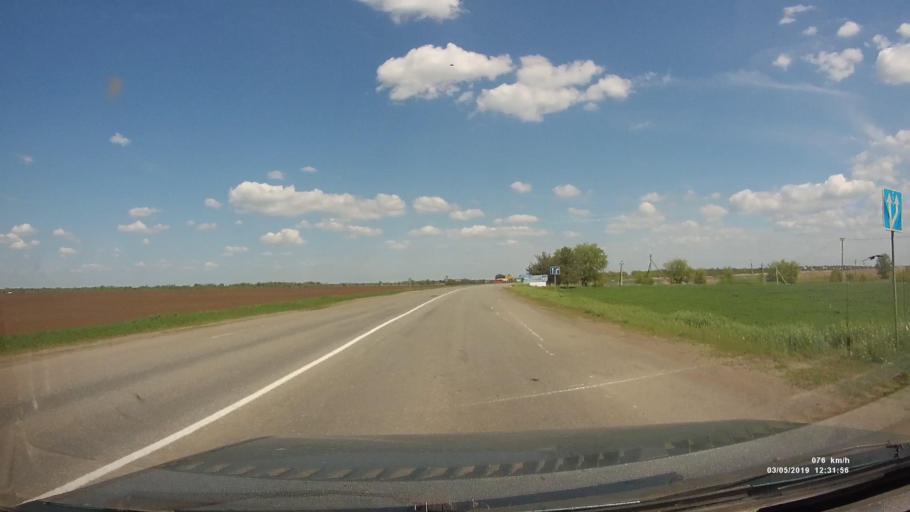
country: RU
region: Rostov
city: Semikarakorsk
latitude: 47.5084
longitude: 40.7525
